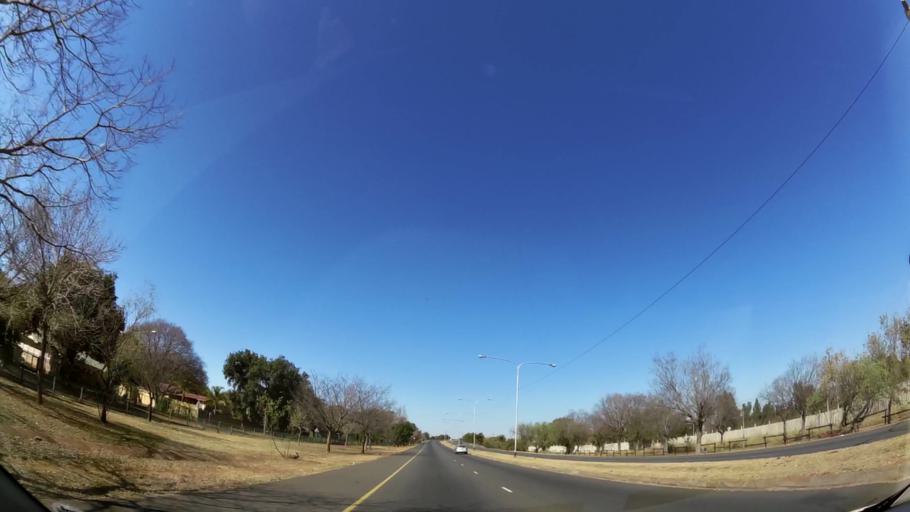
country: ZA
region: Gauteng
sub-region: City of Tshwane Metropolitan Municipality
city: Centurion
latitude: -25.8225
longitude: 28.2054
